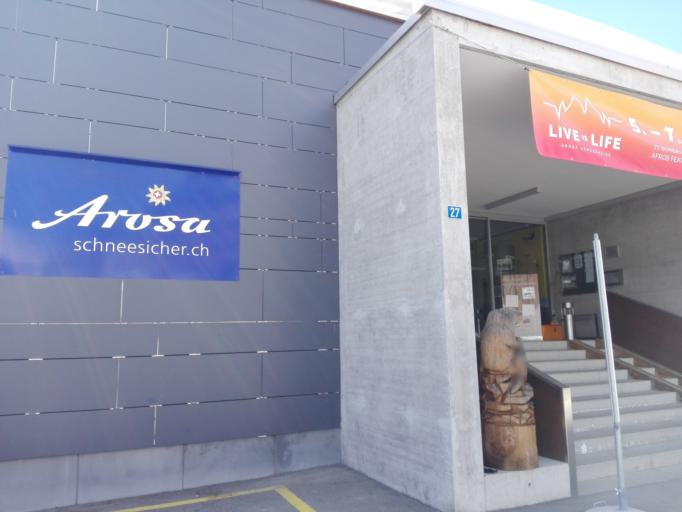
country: CH
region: Grisons
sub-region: Plessur District
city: Arosa
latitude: 46.7828
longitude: 9.6834
